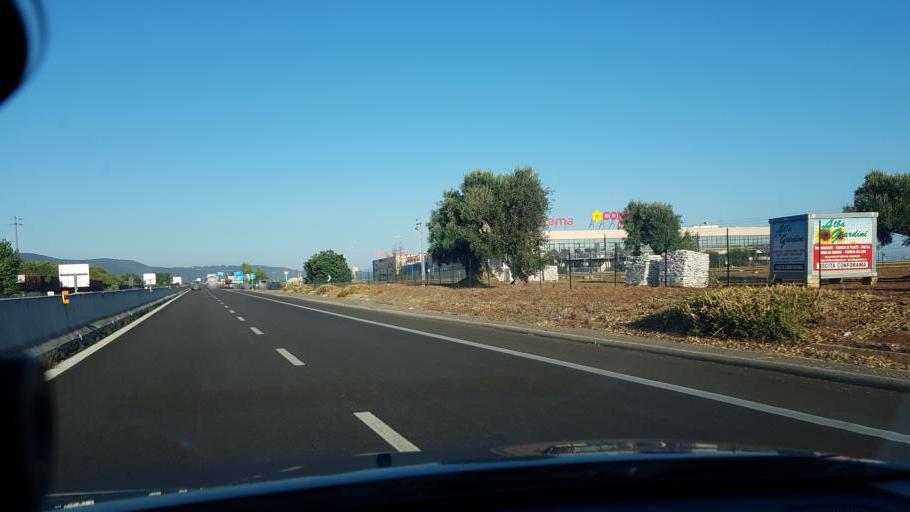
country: IT
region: Apulia
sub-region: Provincia di Brindisi
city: Fasano
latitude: 40.8375
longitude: 17.3815
